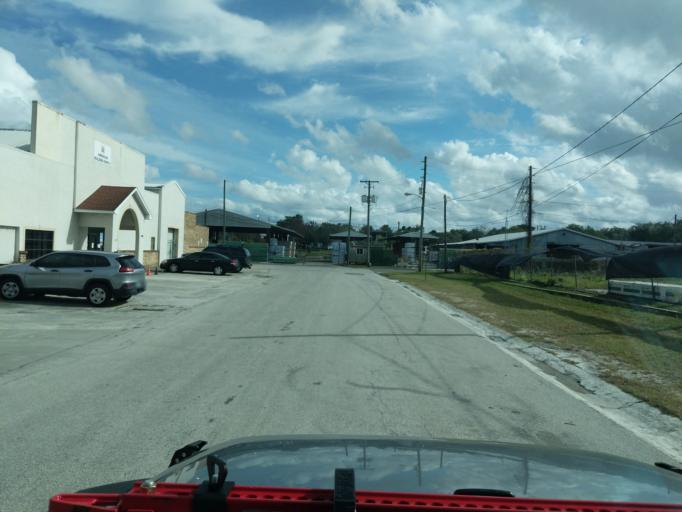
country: US
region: Florida
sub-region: Lake County
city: Clermont
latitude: 28.5580
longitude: -81.7738
